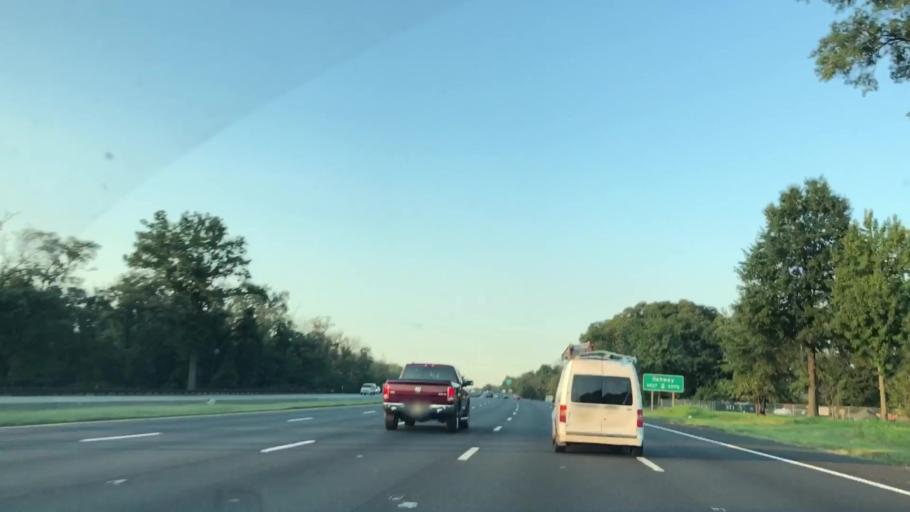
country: US
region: New Jersey
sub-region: Union County
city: Clark
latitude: 40.6331
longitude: -74.2977
